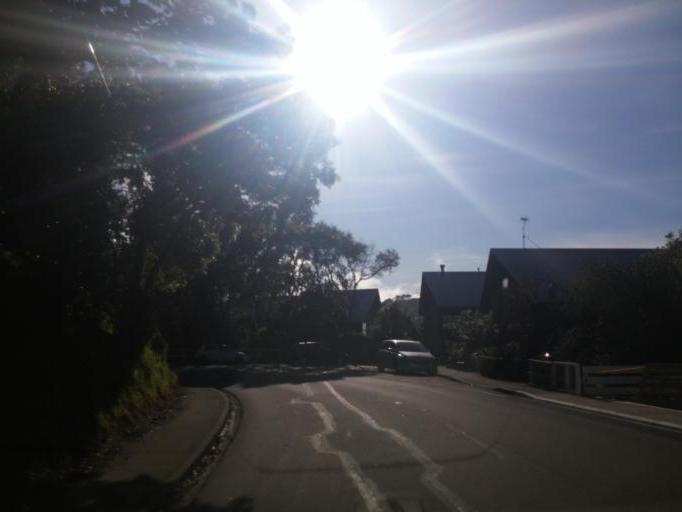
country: NZ
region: Wellington
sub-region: Wellington City
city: Kelburn
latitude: -41.2884
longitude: 174.7562
